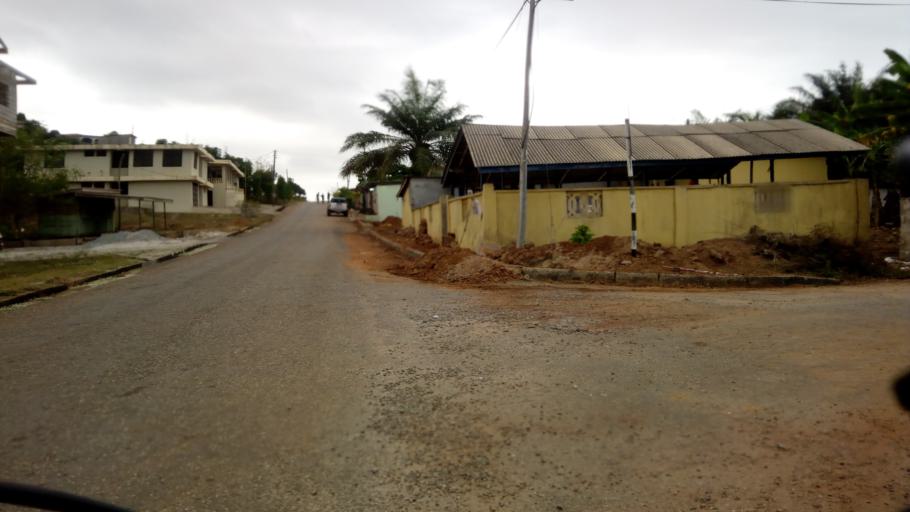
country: GH
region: Central
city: Cape Coast
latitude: 5.1075
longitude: -1.2784
